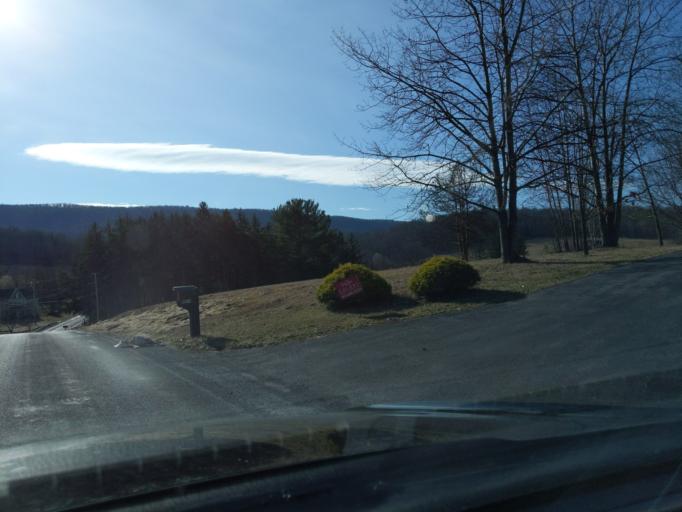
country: US
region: Pennsylvania
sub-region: Blair County
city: Hollidaysburg
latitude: 40.4083
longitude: -78.3235
